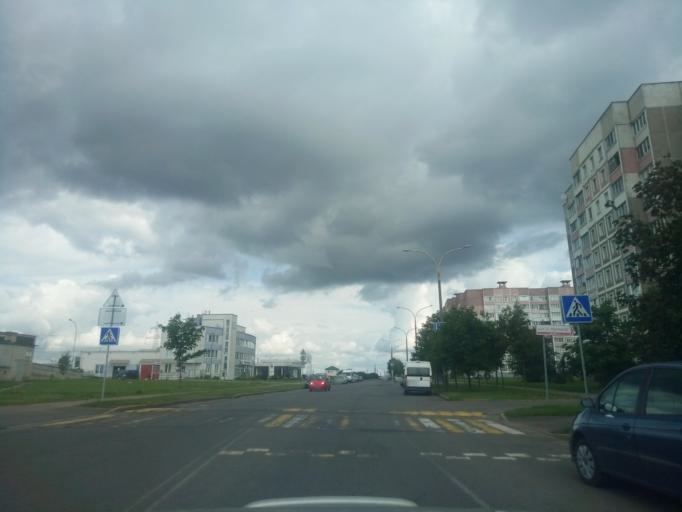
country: BY
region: Minsk
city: Malinovka
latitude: 53.8821
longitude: 27.4188
